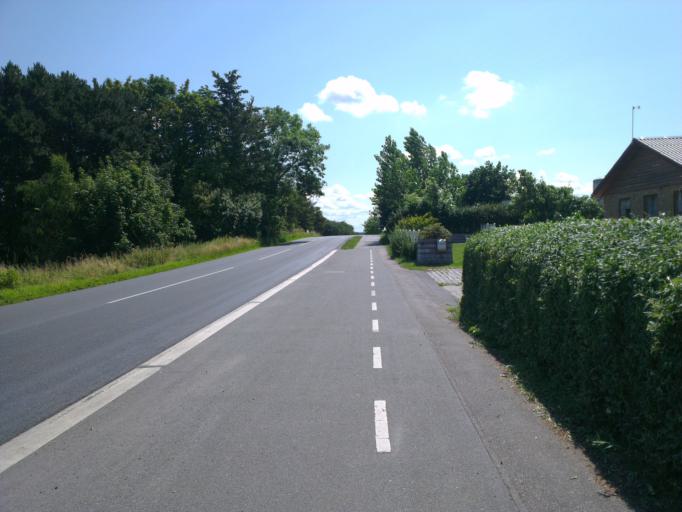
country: DK
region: Capital Region
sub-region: Frederikssund Kommune
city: Skibby
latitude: 55.7693
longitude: 11.9071
